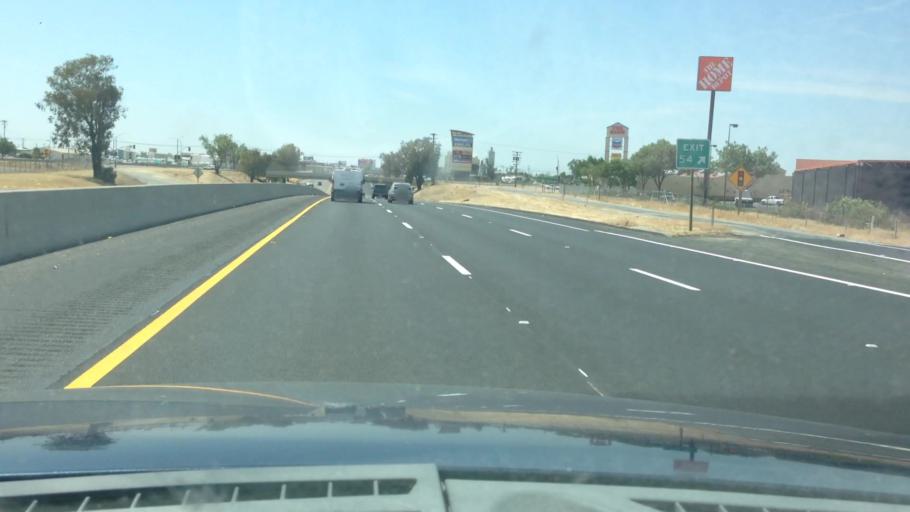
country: US
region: California
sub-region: Kern County
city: Delano
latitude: 35.7497
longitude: -119.2450
